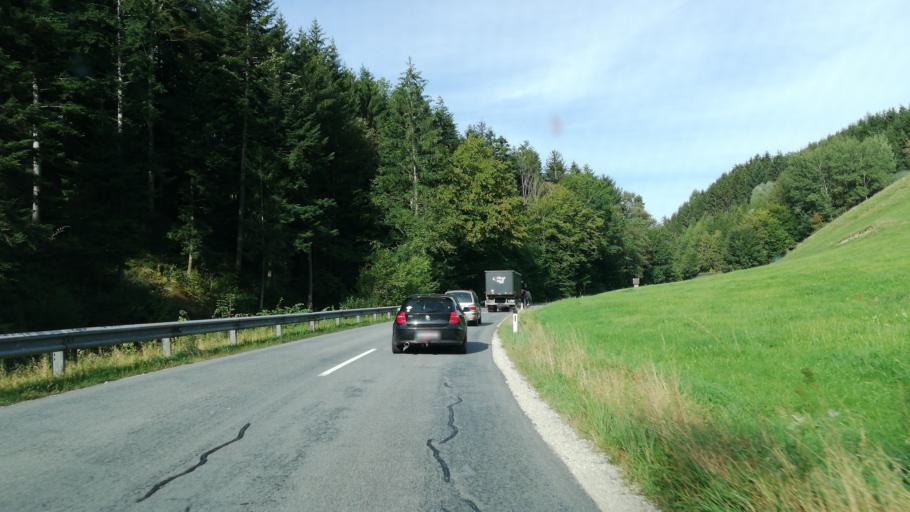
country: AT
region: Lower Austria
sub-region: Politischer Bezirk Amstetten
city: Behamberg
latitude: 47.9900
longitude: 14.5297
